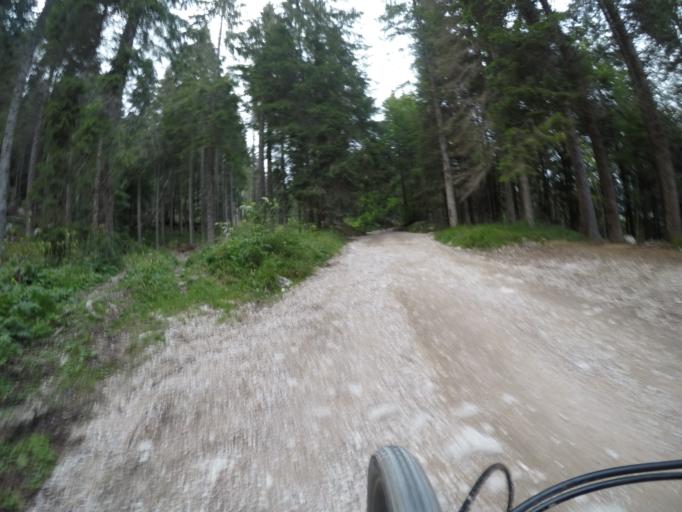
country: IT
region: Veneto
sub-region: Provincia di Vicenza
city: Gallio
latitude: 45.9122
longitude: 11.5242
